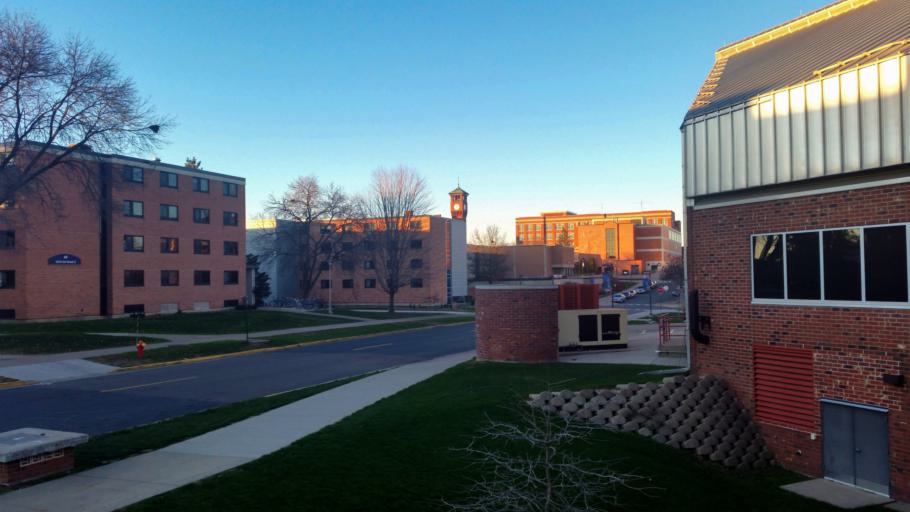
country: US
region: Wisconsin
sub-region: Dunn County
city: Menomonie
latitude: 44.8727
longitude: -91.9269
